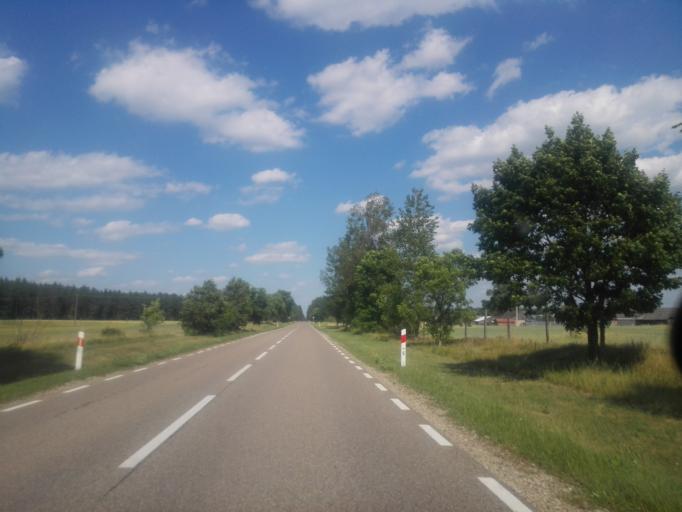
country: PL
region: Podlasie
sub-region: Powiat sejnenski
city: Krasnopol
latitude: 53.9554
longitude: 23.2152
